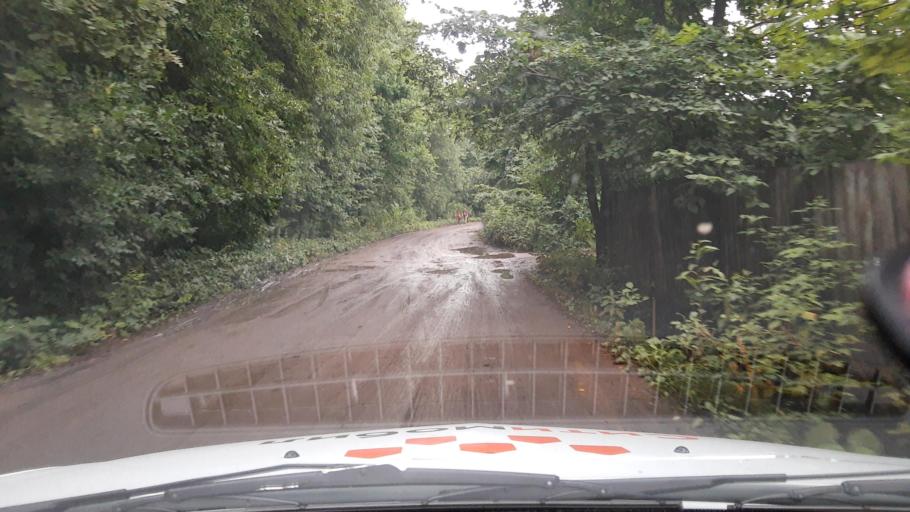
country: RU
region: Bashkortostan
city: Ufa
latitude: 54.5672
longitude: 55.9526
